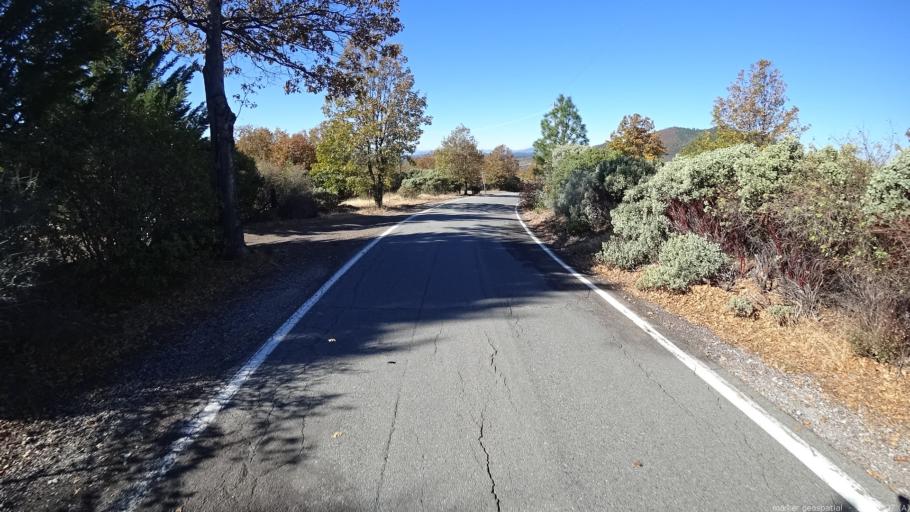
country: US
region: California
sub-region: Shasta County
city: Burney
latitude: 40.7908
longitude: -121.9255
